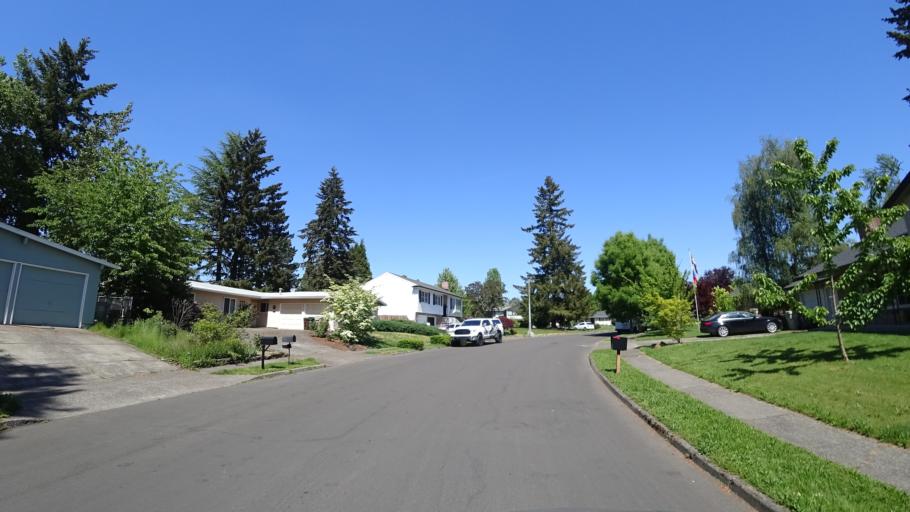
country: US
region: Oregon
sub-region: Washington County
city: Rockcreek
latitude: 45.5488
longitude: -122.8785
